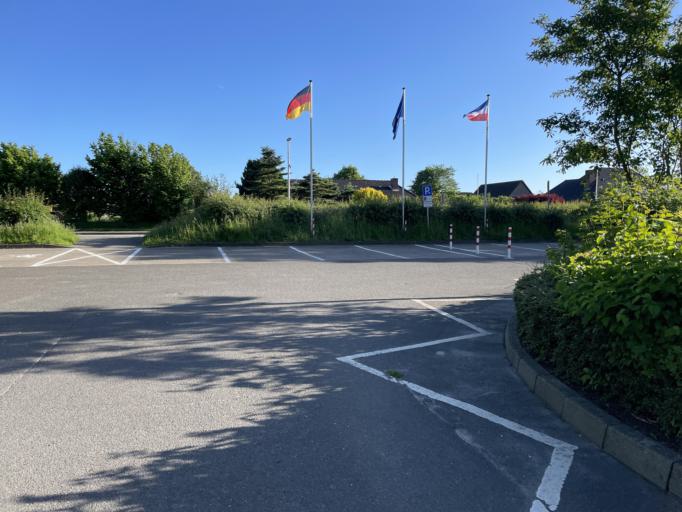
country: DE
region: Schleswig-Holstein
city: Mildstedt
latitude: 54.4600
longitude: 9.0993
